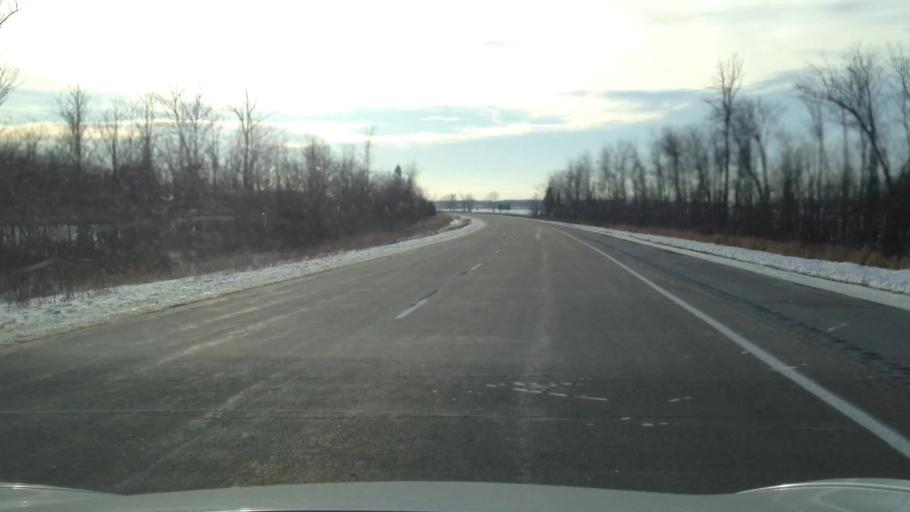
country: CA
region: Ontario
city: Hawkesbury
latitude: 45.4782
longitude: -74.6604
